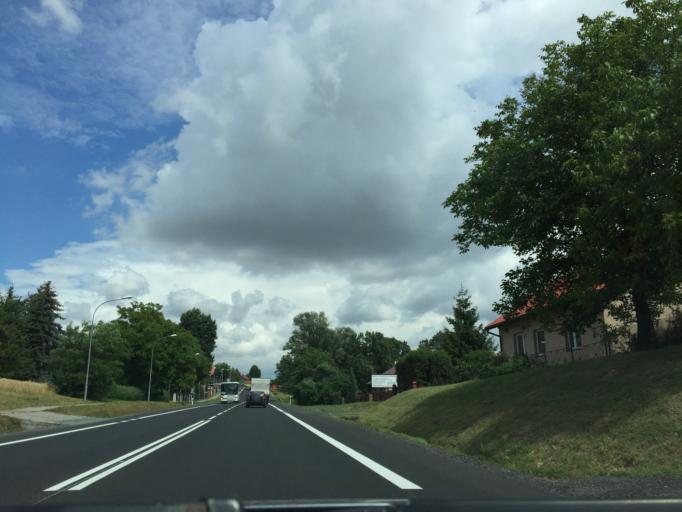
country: PL
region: Lesser Poland Voivodeship
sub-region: Powiat krakowski
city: Michalowice
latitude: 50.2004
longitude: 20.0105
